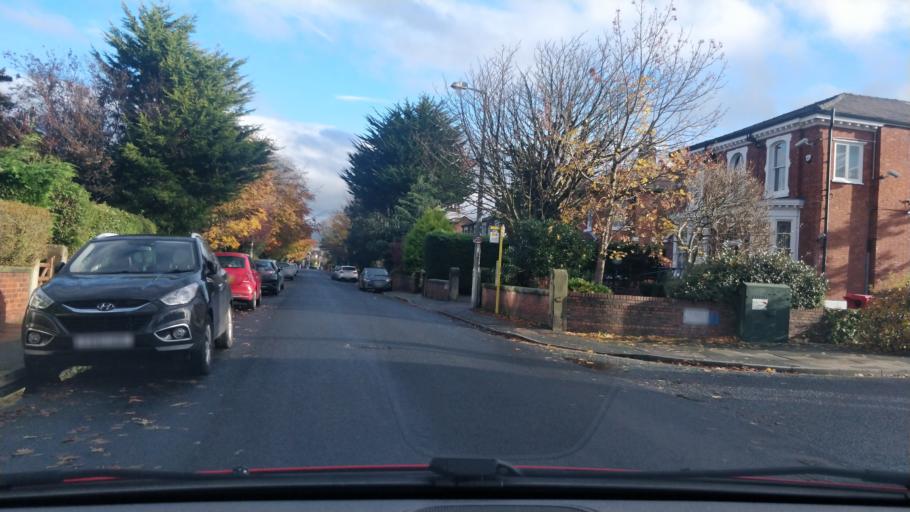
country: GB
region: England
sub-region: Sefton
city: Southport
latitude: 53.6362
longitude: -3.0145
